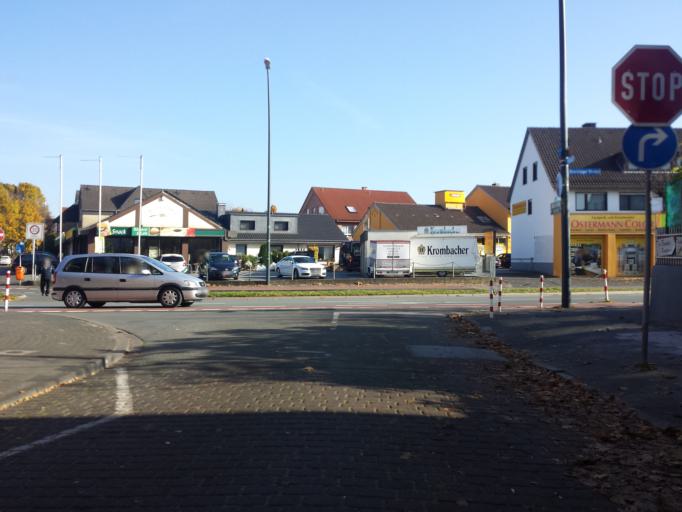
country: DE
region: North Rhine-Westphalia
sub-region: Regierungsbezirk Detmold
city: Guetersloh
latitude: 51.9149
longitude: 8.3714
